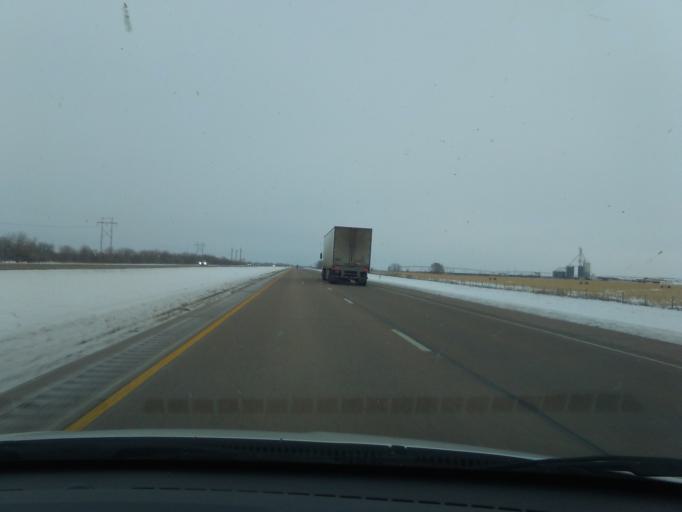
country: US
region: Nebraska
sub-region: Keith County
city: Ogallala
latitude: 41.0870
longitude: -101.8540
